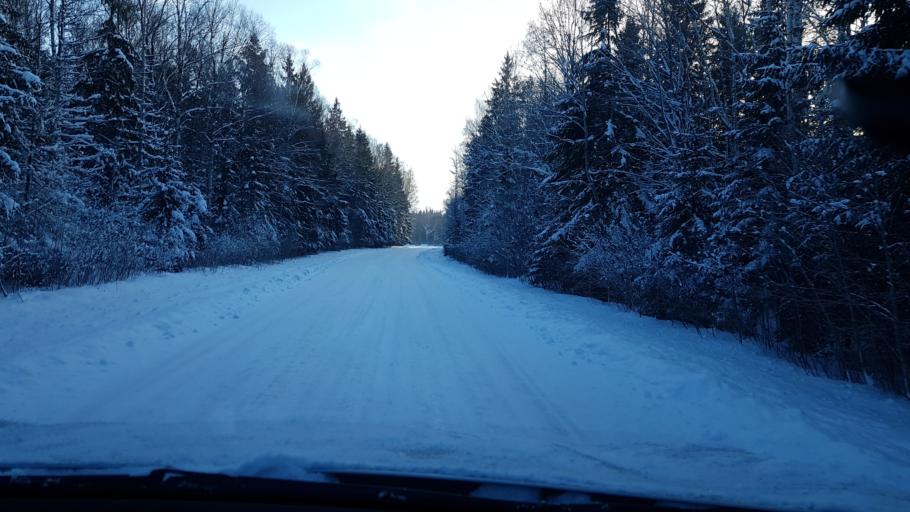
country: EE
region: Harju
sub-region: Nissi vald
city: Turba
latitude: 59.1313
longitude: 24.1959
